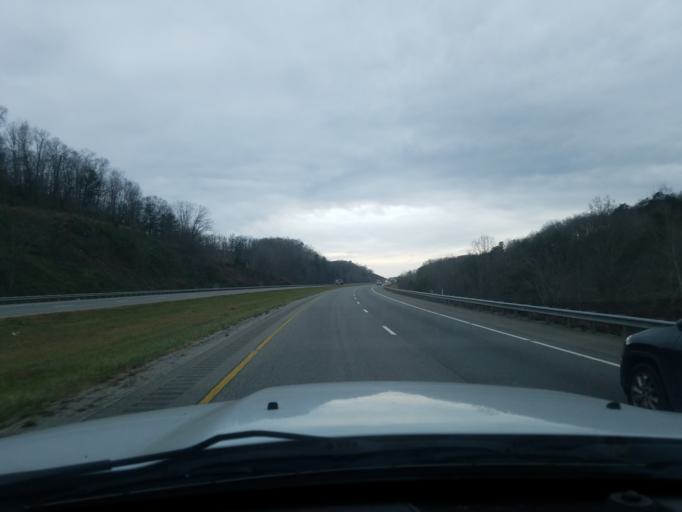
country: US
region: Kentucky
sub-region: Boyd County
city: Meads
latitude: 38.3623
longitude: -82.7363
